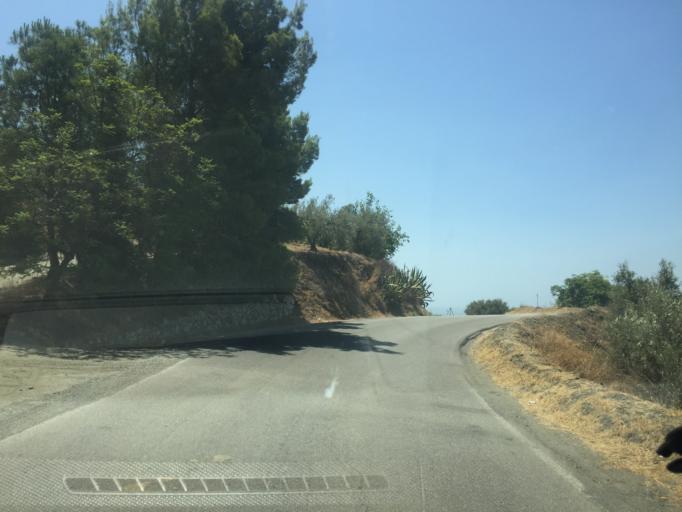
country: ES
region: Andalusia
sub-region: Provincia de Malaga
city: Frigiliana
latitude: 36.8015
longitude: -3.9119
